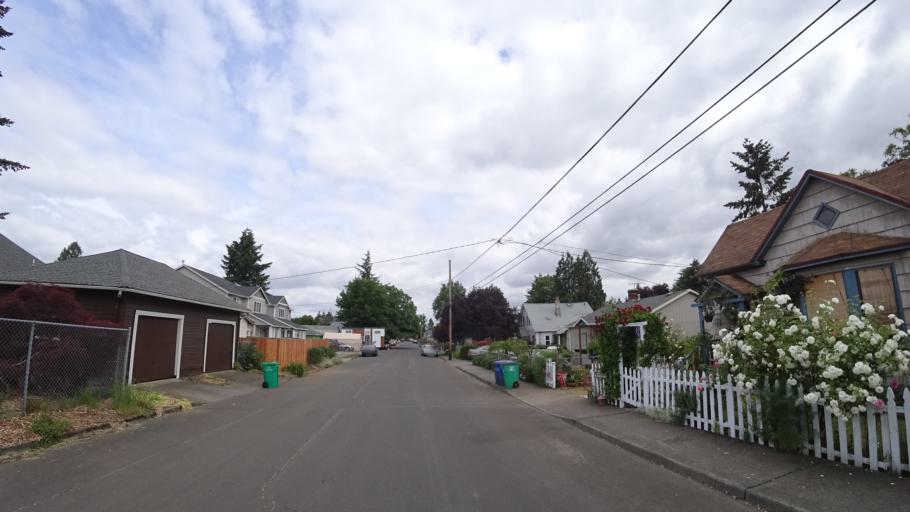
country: US
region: Oregon
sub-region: Multnomah County
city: Lents
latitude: 45.4764
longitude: -122.5765
